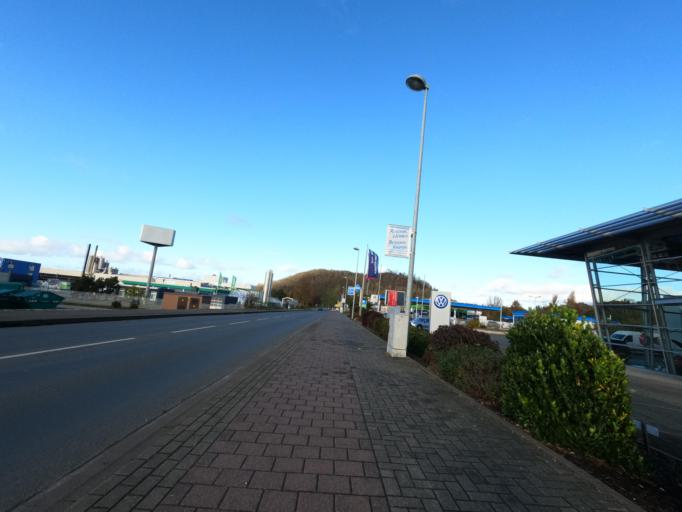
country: DE
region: North Rhine-Westphalia
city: Huckelhoven
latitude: 51.0522
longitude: 6.2181
